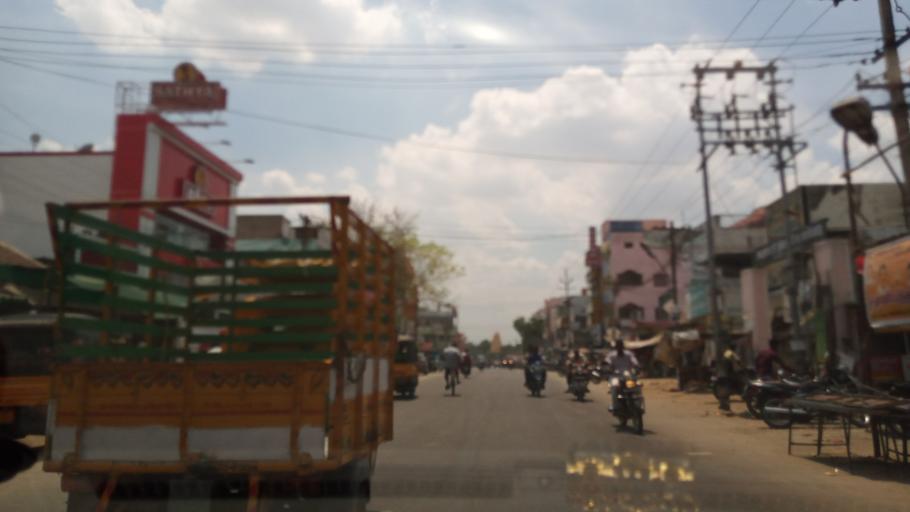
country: IN
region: Tamil Nadu
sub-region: Vellore
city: Walajapet
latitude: 12.9254
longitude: 79.3634
